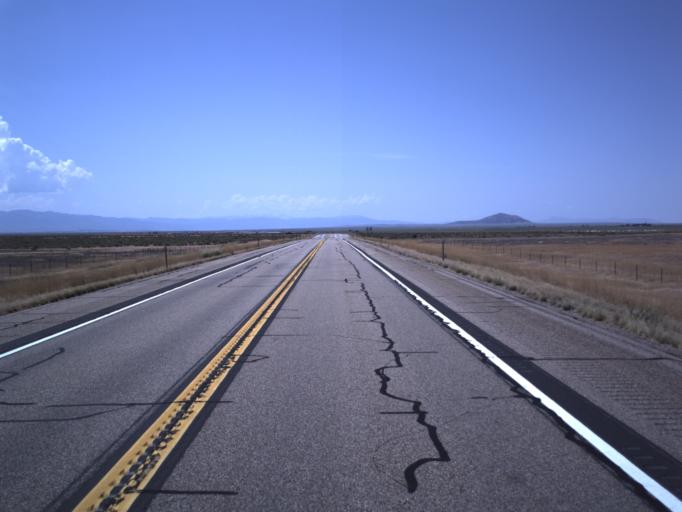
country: US
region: Utah
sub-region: Millard County
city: Delta
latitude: 39.3601
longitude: -112.4965
